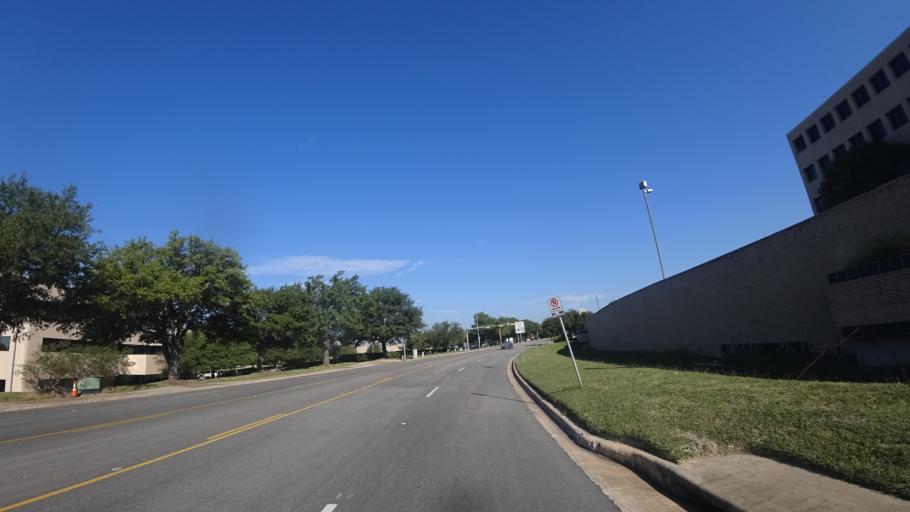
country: US
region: Texas
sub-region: Travis County
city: Austin
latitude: 30.3371
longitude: -97.6761
